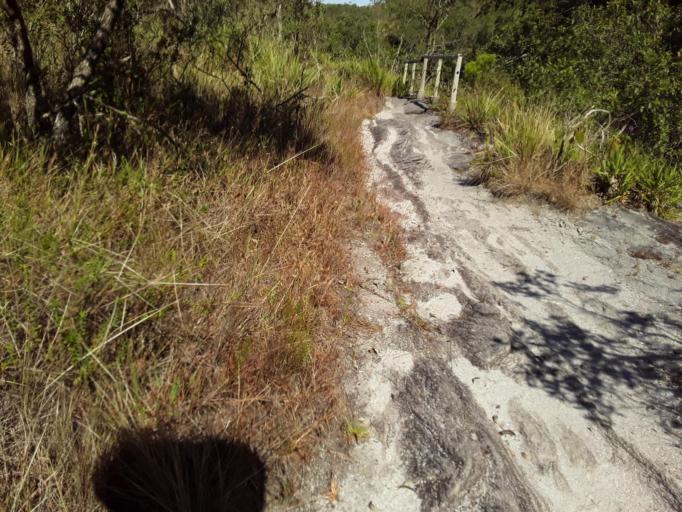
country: BR
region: Minas Gerais
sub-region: Lima Duarte
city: Lima Duarte
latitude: -21.7061
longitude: -43.8940
